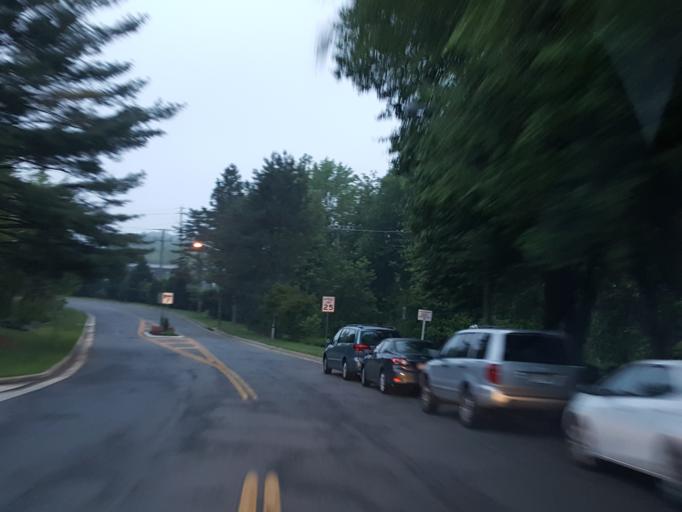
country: US
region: Virginia
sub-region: Fairfax County
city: Annandale
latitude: 38.8381
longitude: -77.2170
